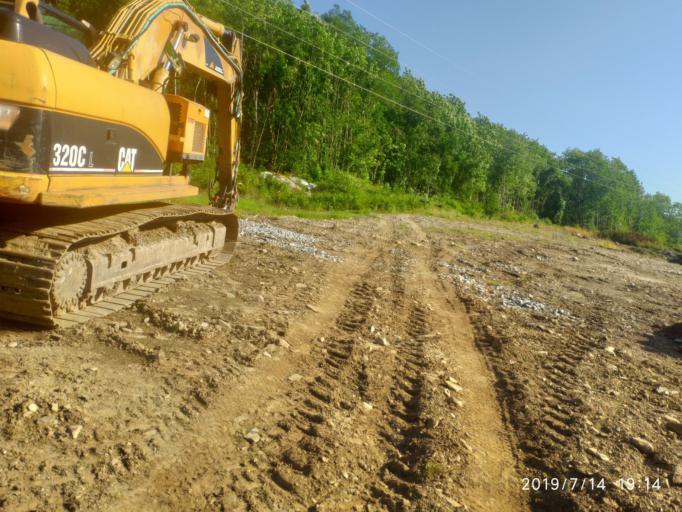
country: NO
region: Hordaland
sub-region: Ullensvang
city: Kinsarvik
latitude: 60.3171
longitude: 6.6597
